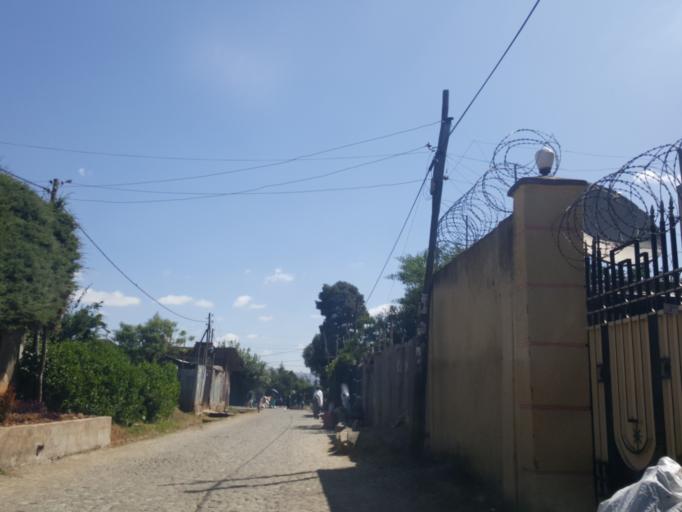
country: ET
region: Adis Abeba
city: Addis Ababa
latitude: 9.0605
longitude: 38.7323
